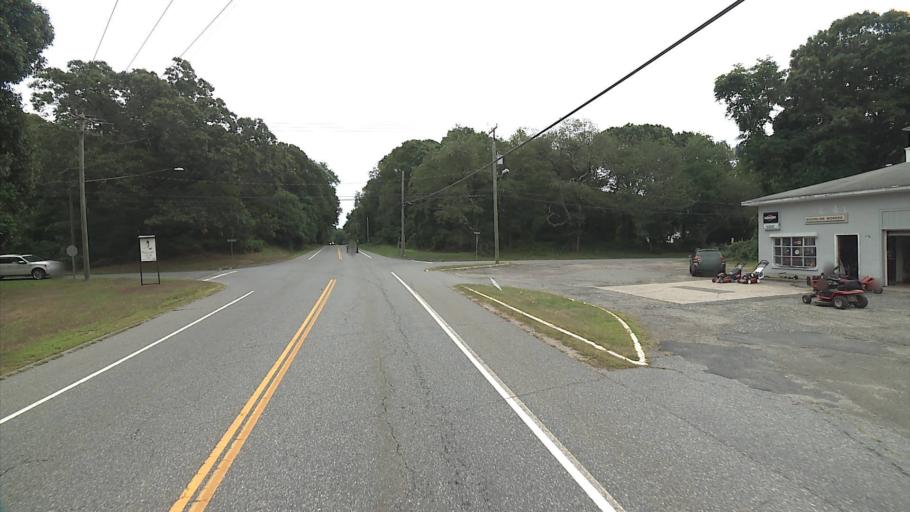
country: US
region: Connecticut
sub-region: Middlesex County
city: Old Saybrook Center
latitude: 41.2866
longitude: -72.3069
